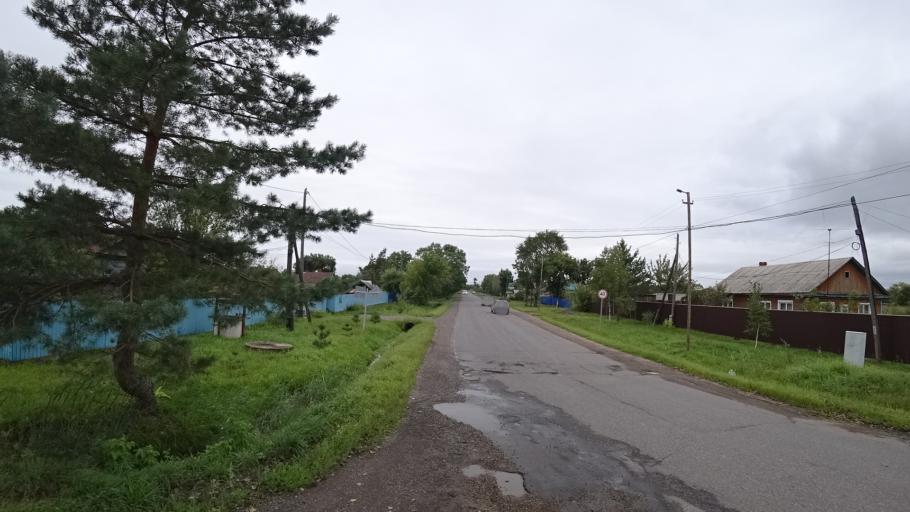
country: RU
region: Primorskiy
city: Chernigovka
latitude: 44.3447
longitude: 132.5681
